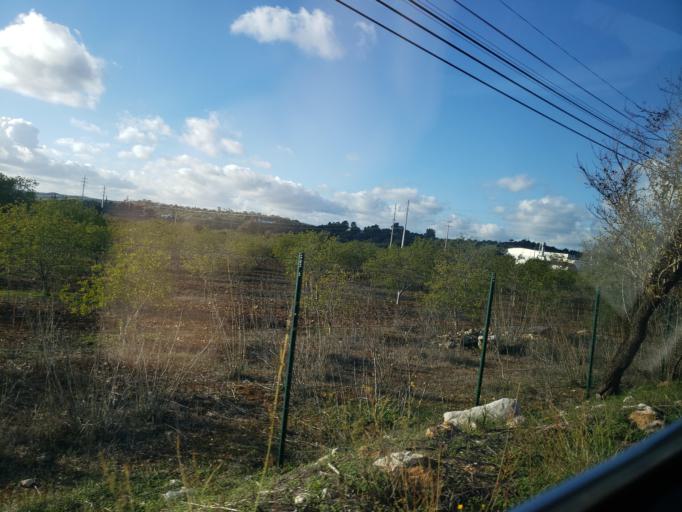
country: PT
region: Faro
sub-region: Portimao
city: Alvor
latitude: 37.1872
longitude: -8.5874
